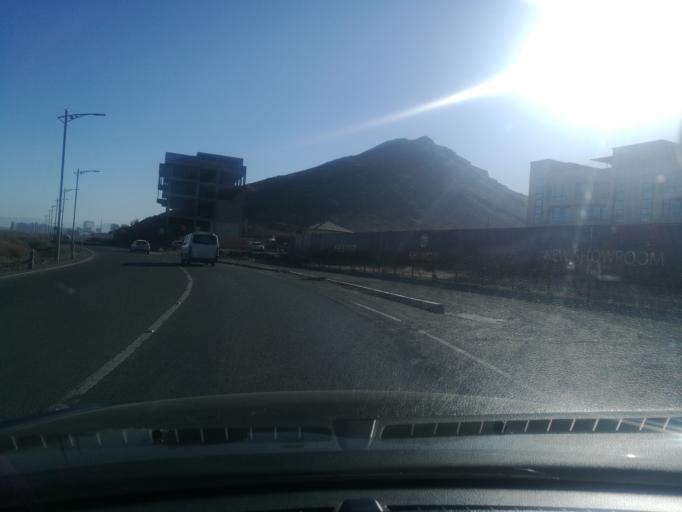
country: MN
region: Ulaanbaatar
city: Ulaanbaatar
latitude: 47.8860
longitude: 106.8782
